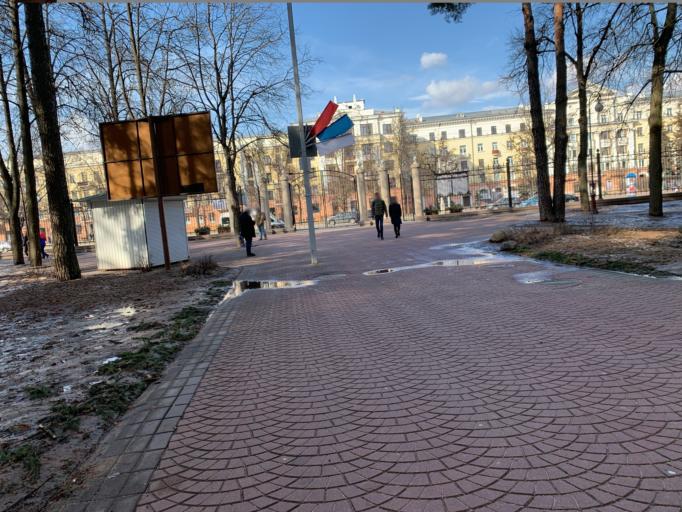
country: BY
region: Minsk
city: Minsk
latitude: 53.9230
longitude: 27.6112
